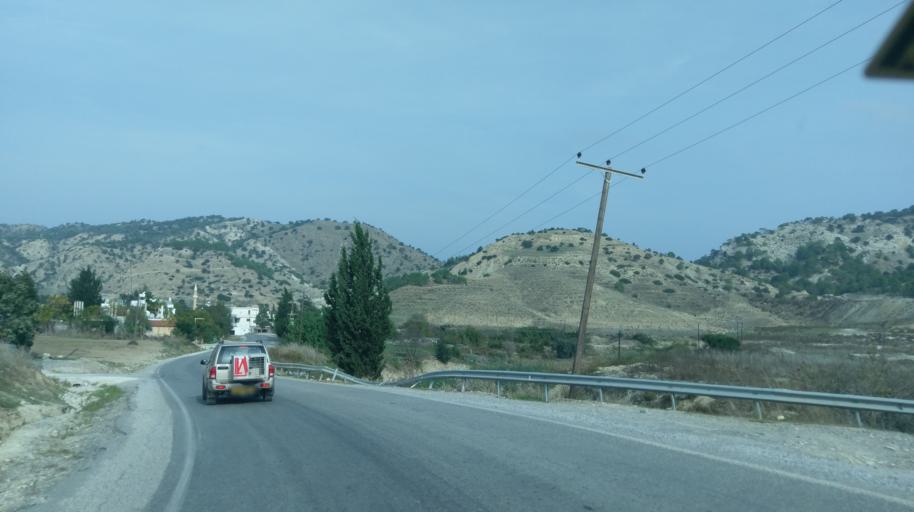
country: CY
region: Keryneia
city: Lapithos
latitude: 35.3311
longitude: 33.0692
